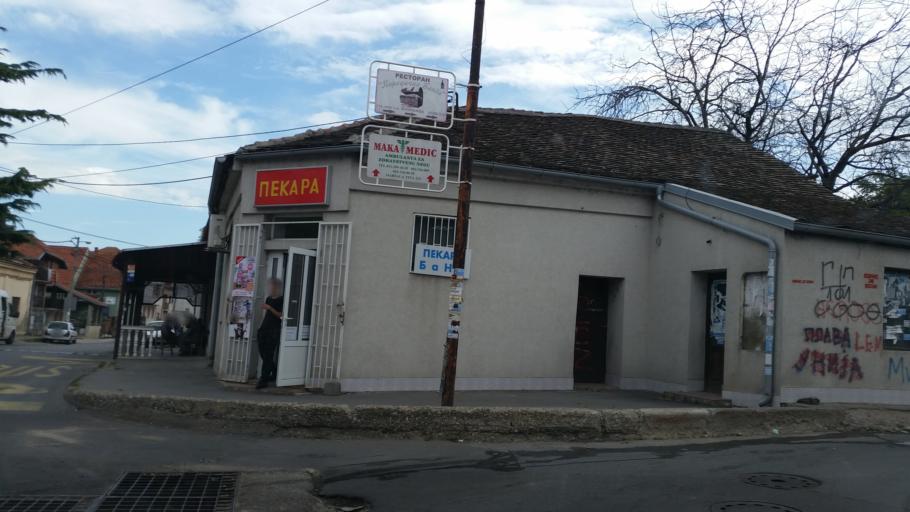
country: RS
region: Central Serbia
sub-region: Belgrade
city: Palilula
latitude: 44.8307
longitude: 20.5480
